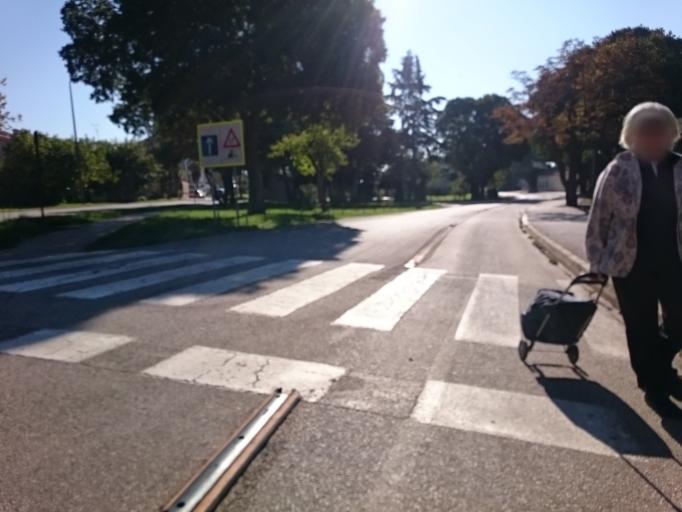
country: HR
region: Istarska
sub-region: Grad Porec
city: Porec
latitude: 45.2329
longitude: 13.5996
